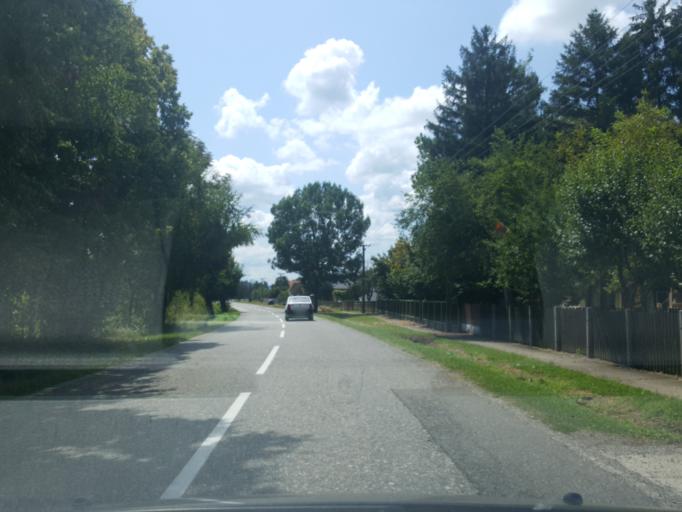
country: RS
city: Zminjak
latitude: 44.7437
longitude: 19.4685
